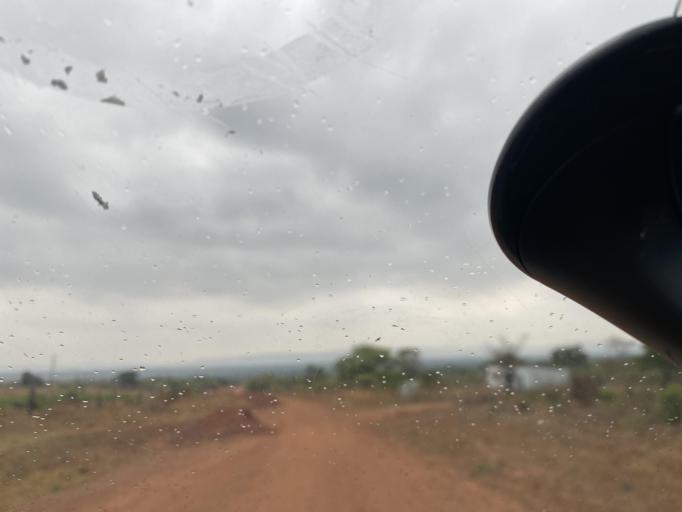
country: ZM
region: Lusaka
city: Chongwe
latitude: -15.1711
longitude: 28.7642
